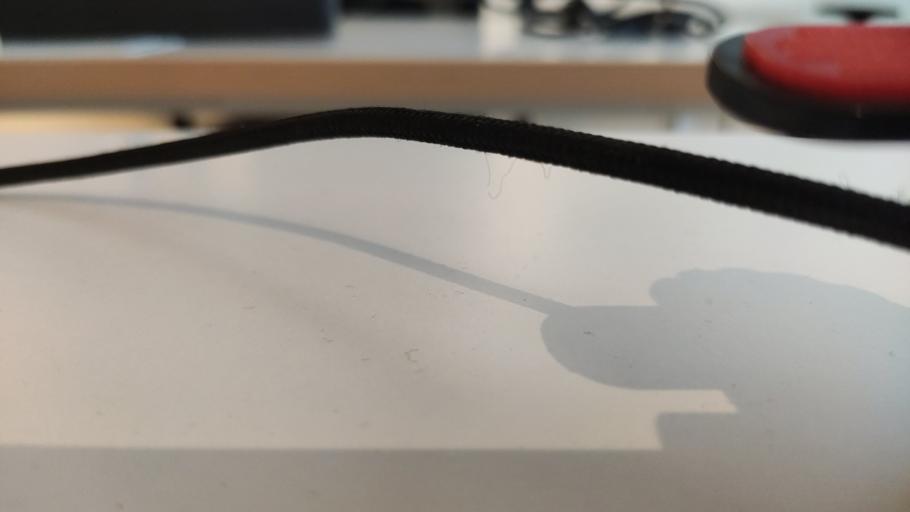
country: RU
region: Moskovskaya
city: Novopetrovskoye
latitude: 55.9607
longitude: 36.4396
